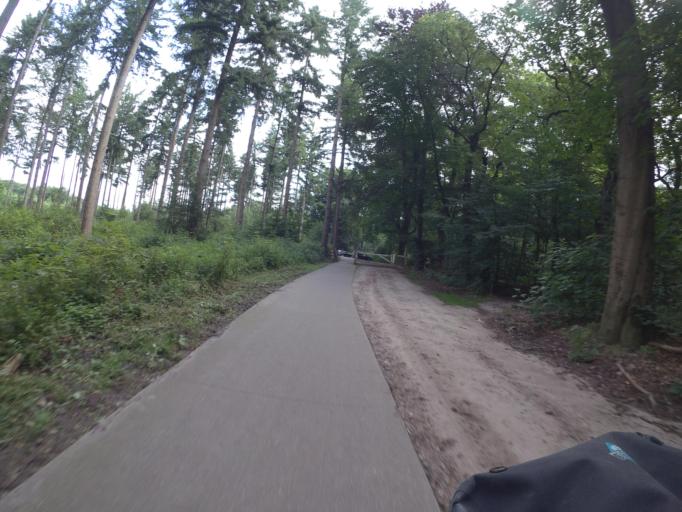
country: NL
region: Gelderland
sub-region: Gemeente Epe
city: Emst
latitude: 52.3463
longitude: 5.9172
